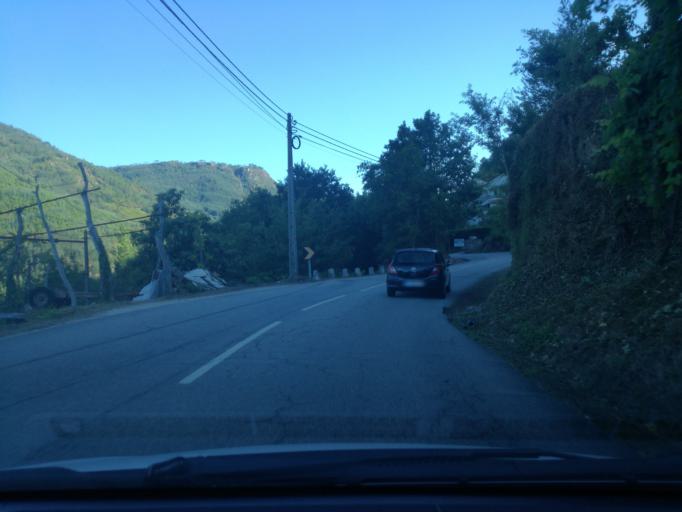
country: PT
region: Braga
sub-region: Vieira do Minho
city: Real
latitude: 41.7054
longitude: -8.1672
